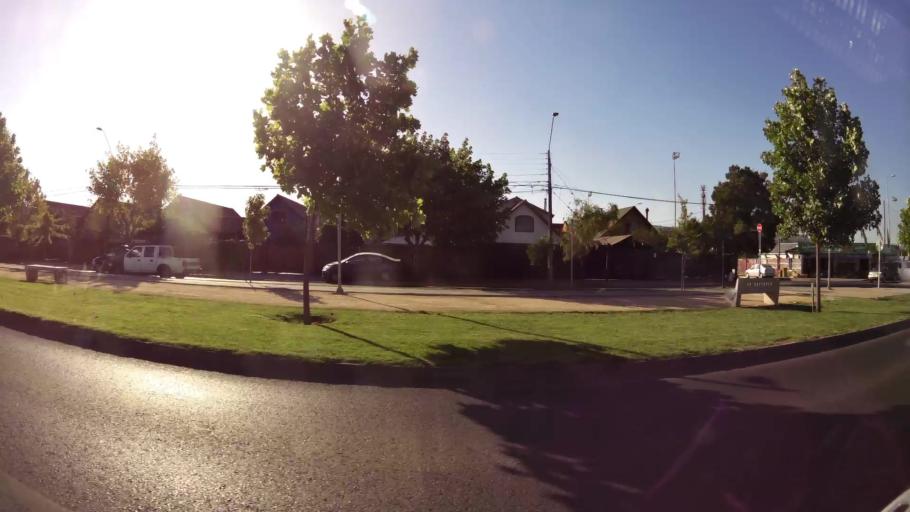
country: CL
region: Maule
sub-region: Provincia de Talca
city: Talca
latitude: -35.4413
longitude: -71.6844
